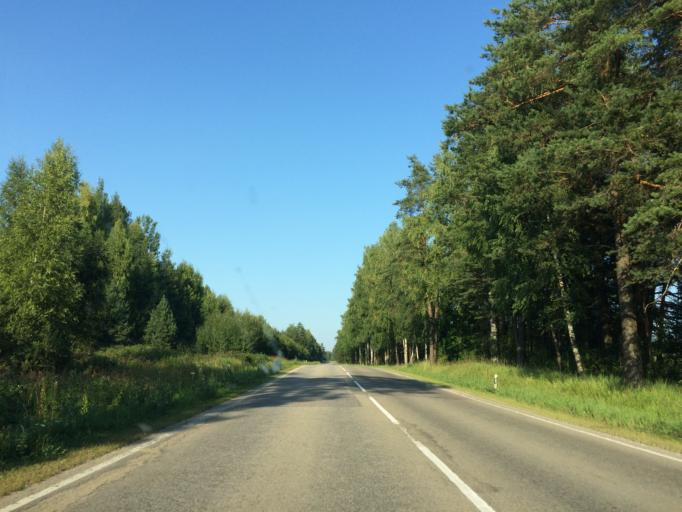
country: LV
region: Ludzas Rajons
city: Ludza
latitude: 56.5337
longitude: 27.5538
